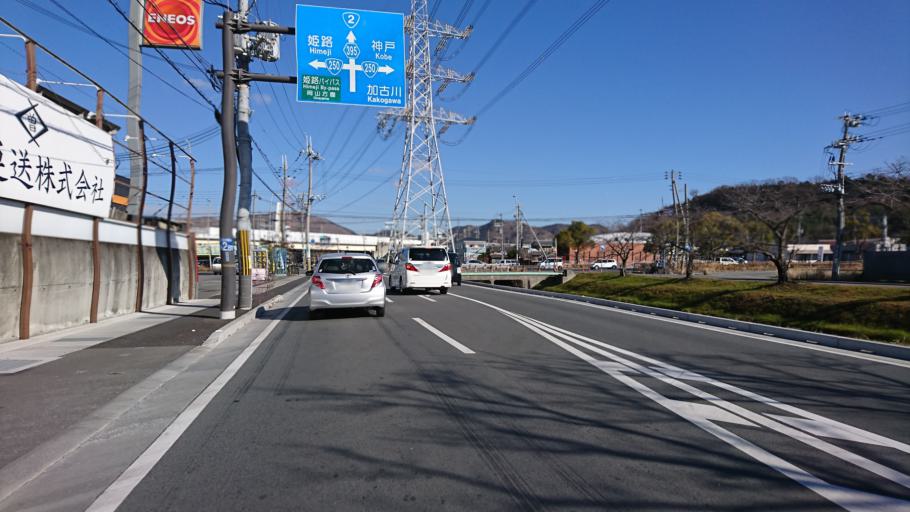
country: JP
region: Hyogo
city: Kakogawacho-honmachi
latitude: 34.7841
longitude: 134.7822
